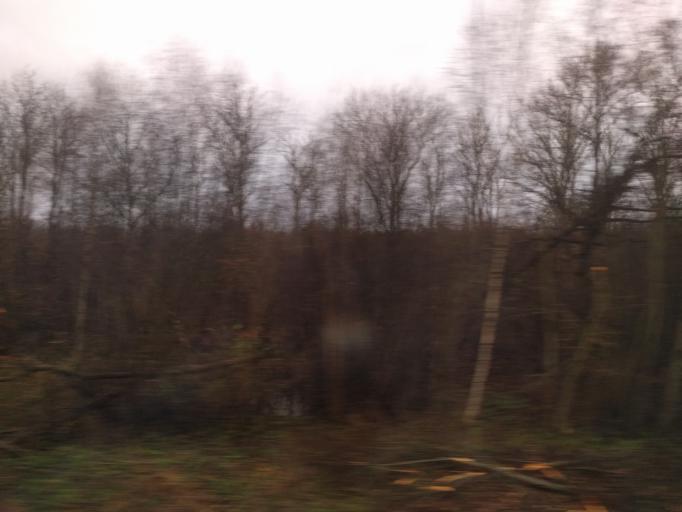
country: DK
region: Zealand
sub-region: Koge Kommune
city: Borup
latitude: 55.5077
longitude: 11.9746
